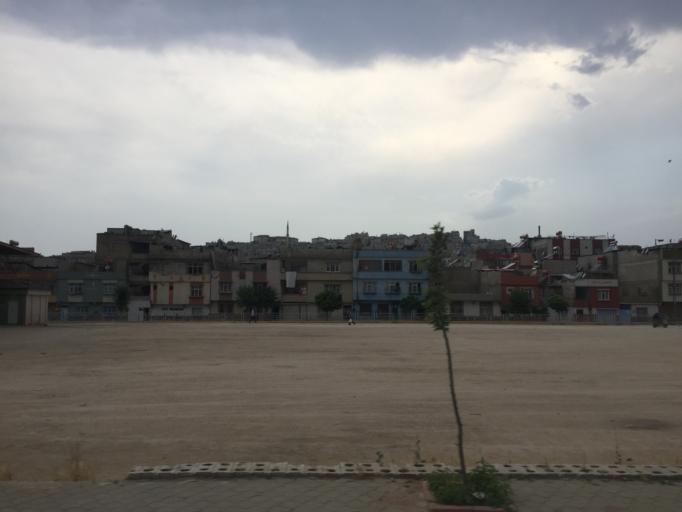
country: TR
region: Gaziantep
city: Gaziantep
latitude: 37.0703
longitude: 37.4136
